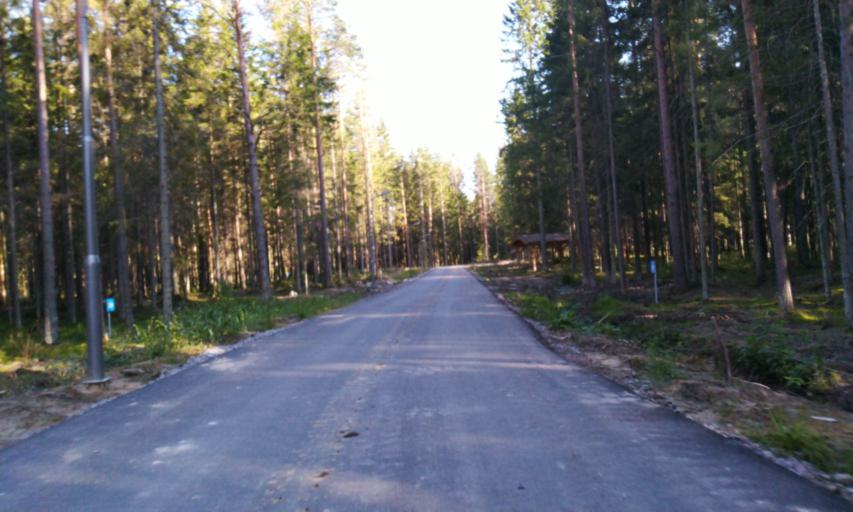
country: RU
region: Leningrad
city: Toksovo
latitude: 60.1314
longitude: 30.4584
